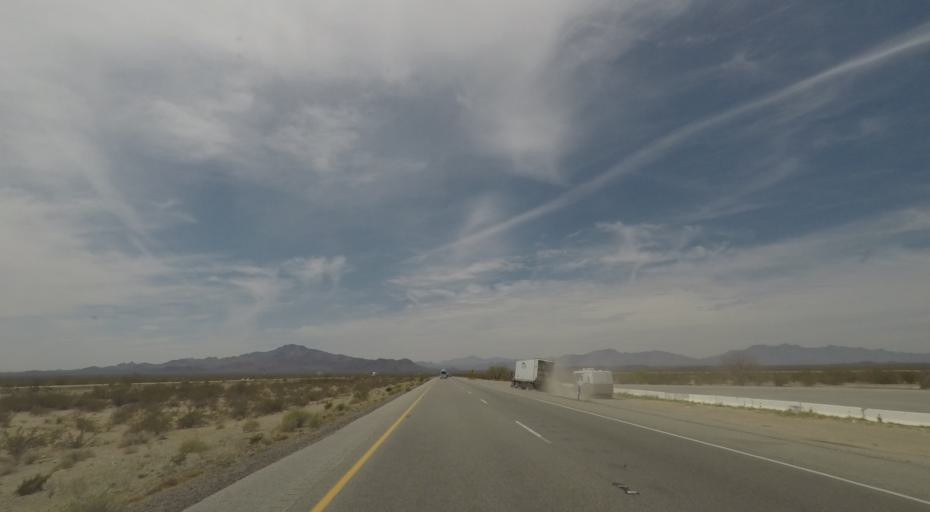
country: US
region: California
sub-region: San Bernardino County
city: Needles
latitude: 34.8096
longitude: -115.2194
